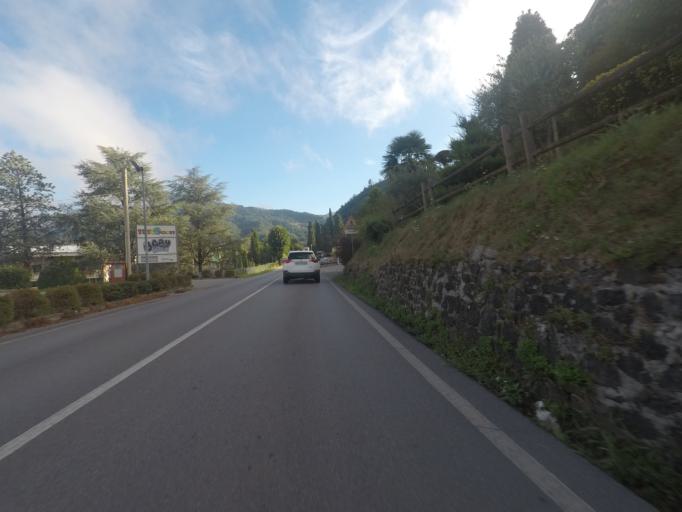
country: IT
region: Tuscany
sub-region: Provincia di Lucca
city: Bagni di Lucca
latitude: 43.9975
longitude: 10.5572
